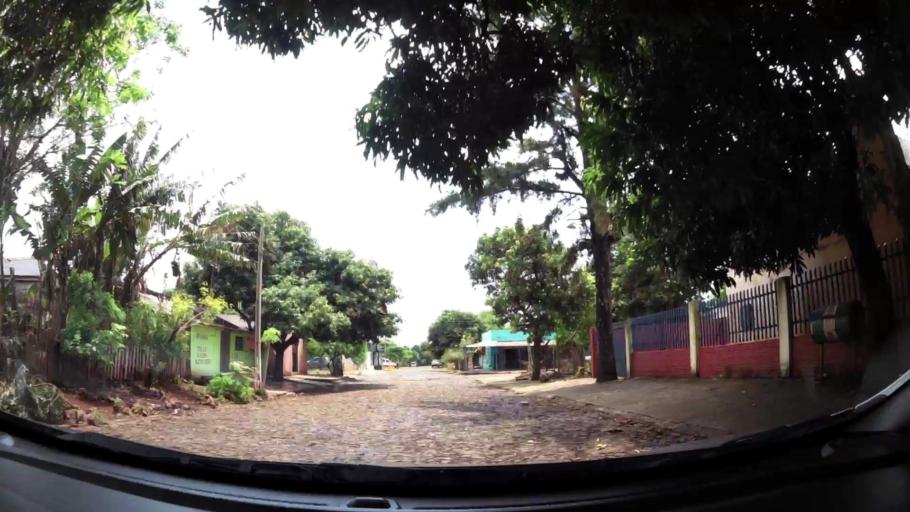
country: PY
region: Alto Parana
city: Ciudad del Este
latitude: -25.5044
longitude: -54.6613
